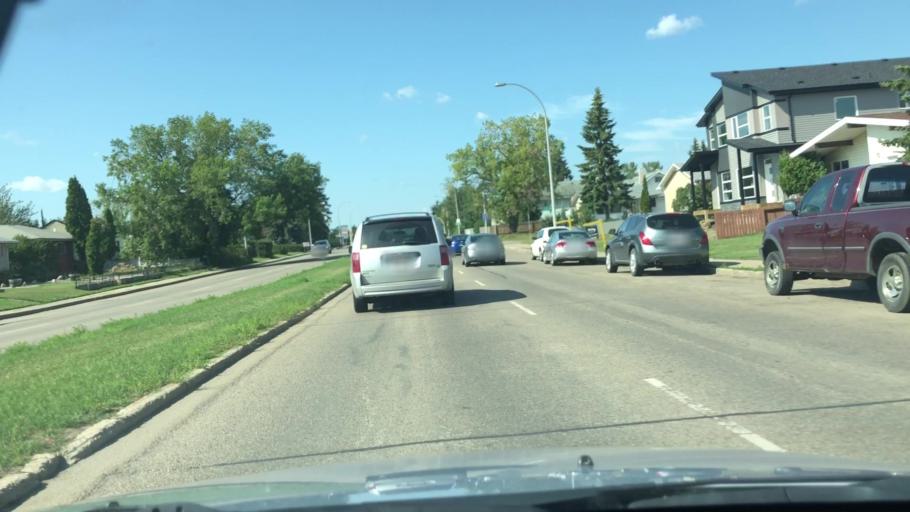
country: CA
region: Alberta
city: Edmonton
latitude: 53.5932
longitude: -113.4429
